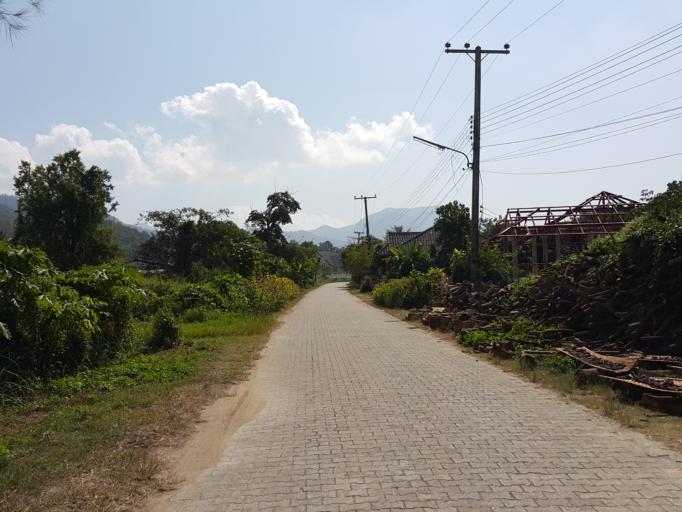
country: TH
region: Chiang Mai
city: Mae On
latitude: 18.7159
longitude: 99.2014
